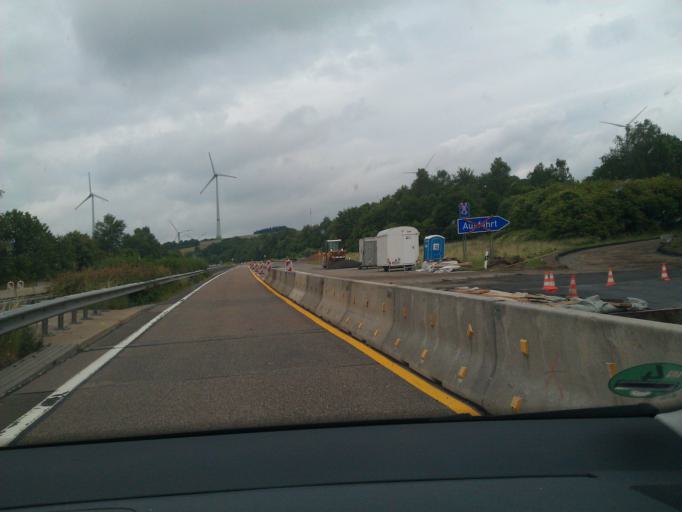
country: DE
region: Saarland
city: Freisen
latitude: 49.5520
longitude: 7.2574
